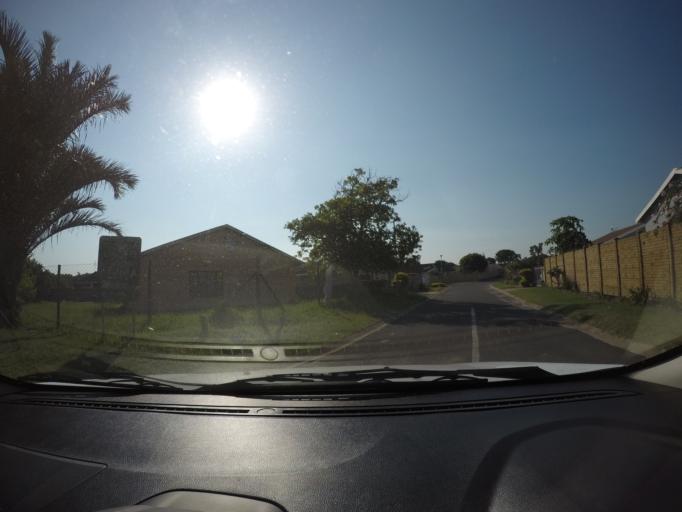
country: ZA
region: KwaZulu-Natal
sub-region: uThungulu District Municipality
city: Richards Bay
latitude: -28.7159
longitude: 32.0337
